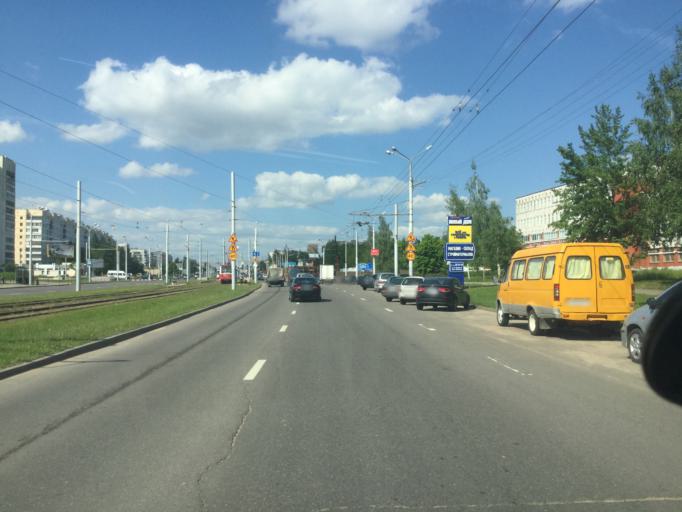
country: BY
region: Vitebsk
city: Vitebsk
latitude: 55.1663
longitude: 30.2409
